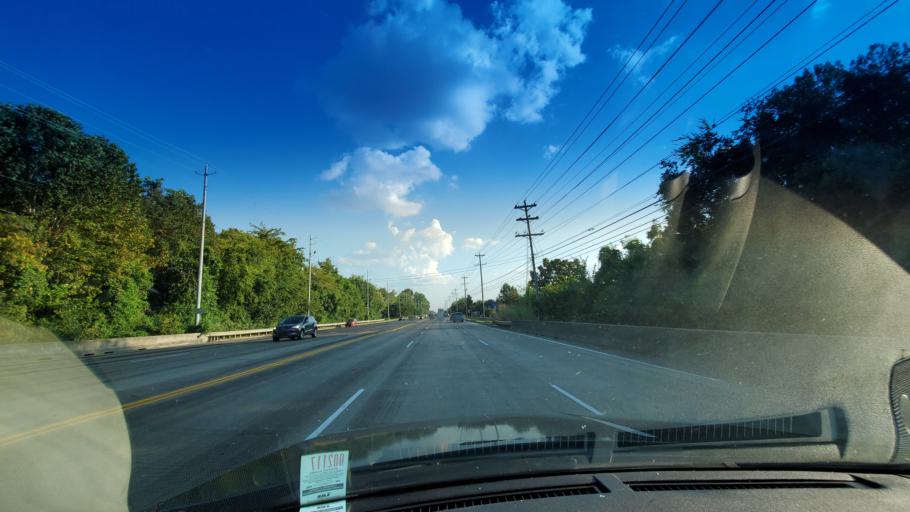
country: US
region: Tennessee
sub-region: Rutherford County
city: Murfreesboro
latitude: 35.8043
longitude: -86.3979
